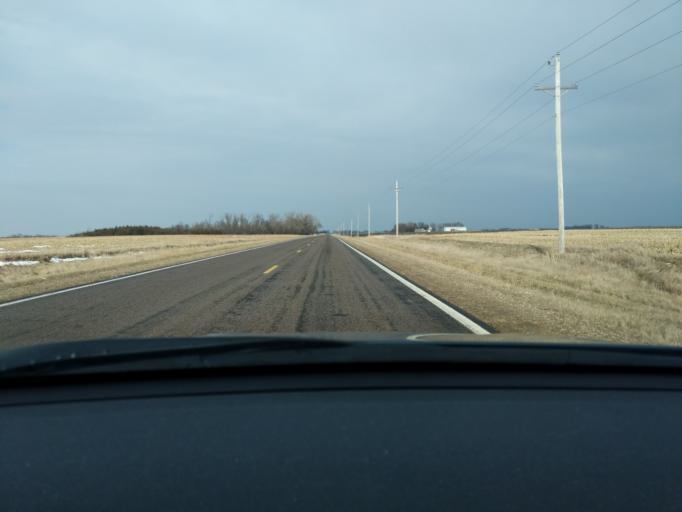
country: US
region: Minnesota
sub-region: Renville County
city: Renville
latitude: 44.7507
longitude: -95.3407
